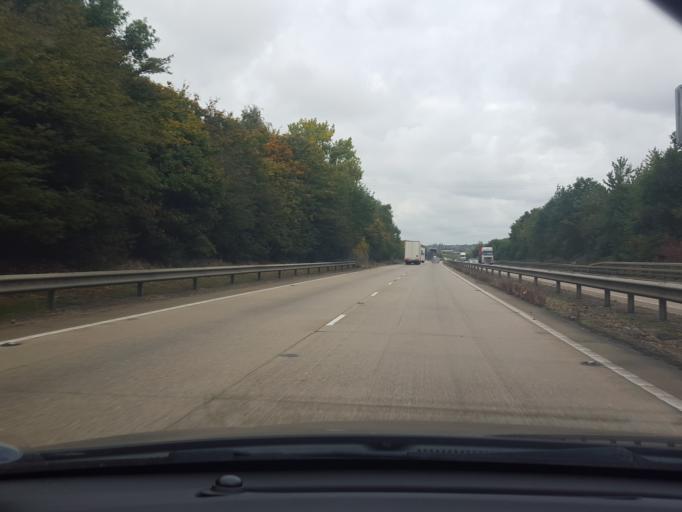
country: GB
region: England
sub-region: Suffolk
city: Bramford
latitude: 52.0499
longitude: 1.0980
